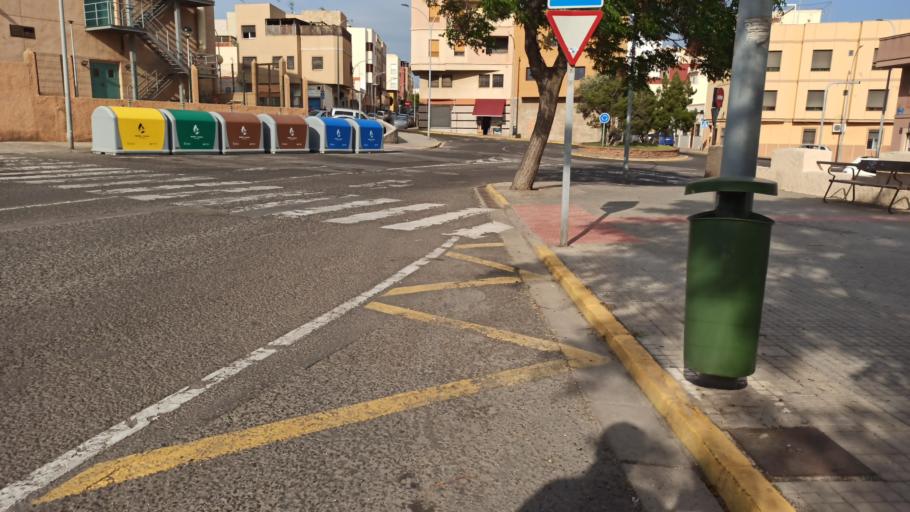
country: ES
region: Melilla
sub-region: Melilla
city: Melilla
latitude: 35.2841
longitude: -2.9486
